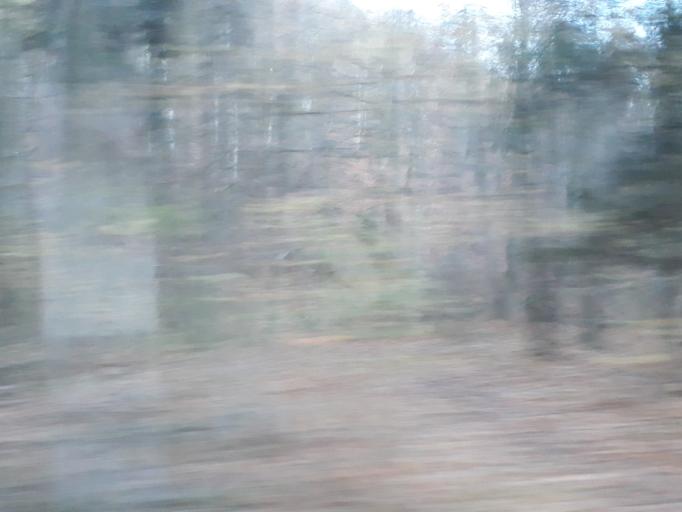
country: DE
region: Saxony
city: Kreischa
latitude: 50.9233
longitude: 13.7789
